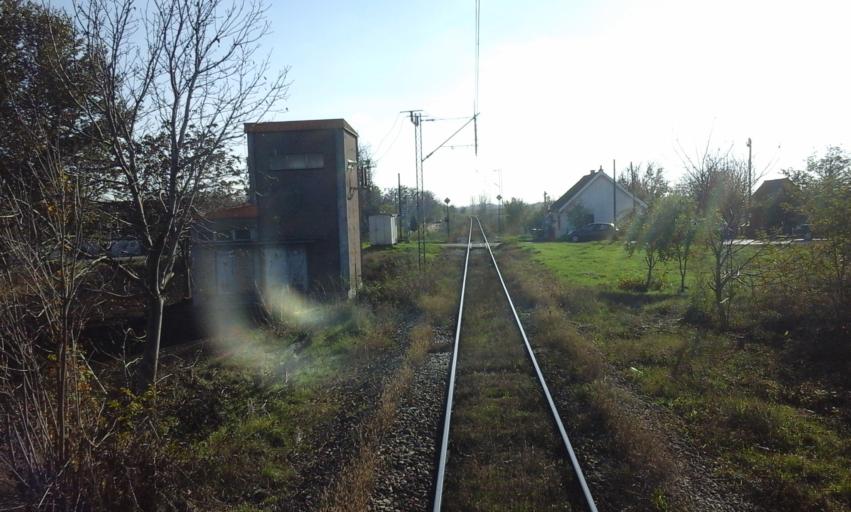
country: RS
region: Autonomna Pokrajina Vojvodina
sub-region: Severnobacki Okrug
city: Backa Topola
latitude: 45.8054
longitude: 19.6476
